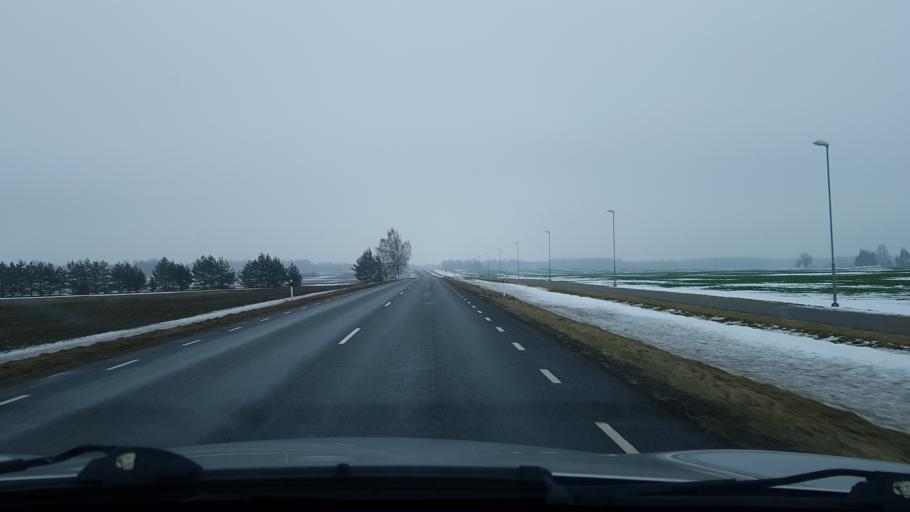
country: EE
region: Valgamaa
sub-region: Torva linn
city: Torva
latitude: 58.2203
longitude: 25.9000
